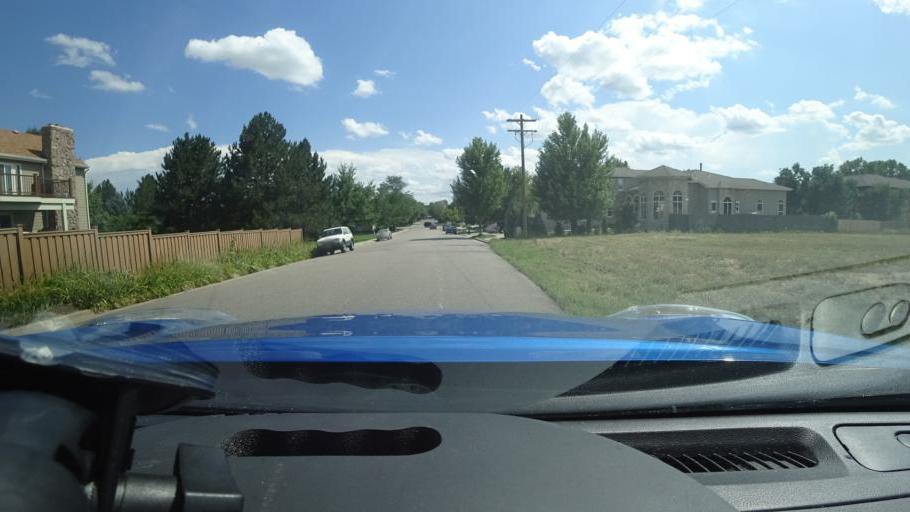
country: US
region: Colorado
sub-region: Adams County
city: Aurora
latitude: 39.6778
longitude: -104.8613
